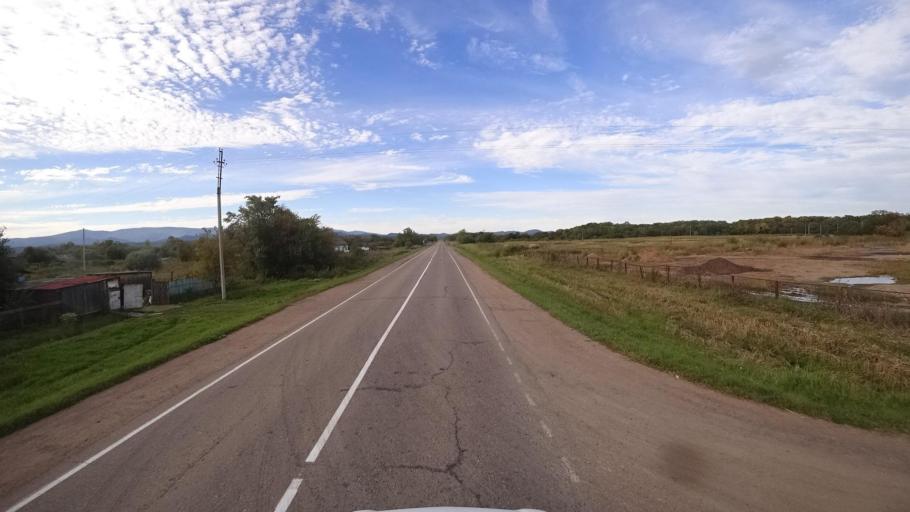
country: RU
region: Primorskiy
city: Dostoyevka
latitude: 44.2982
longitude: 133.4262
